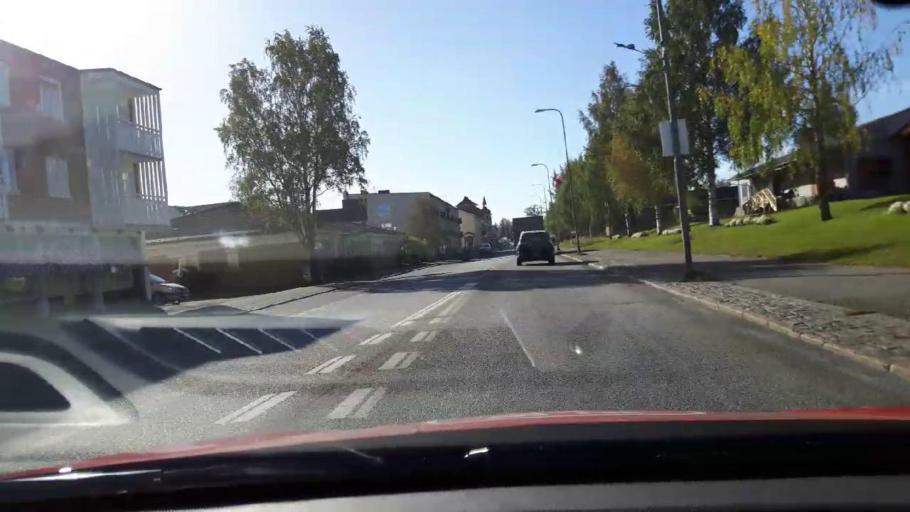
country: SE
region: Jaemtland
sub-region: Braecke Kommun
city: Braecke
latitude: 62.7530
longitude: 15.4166
